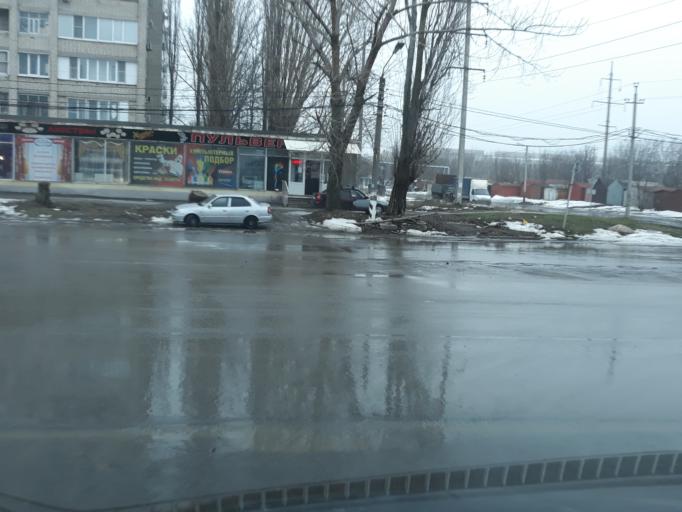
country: RU
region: Rostov
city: Novobessergenovka
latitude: 47.2158
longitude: 38.8632
